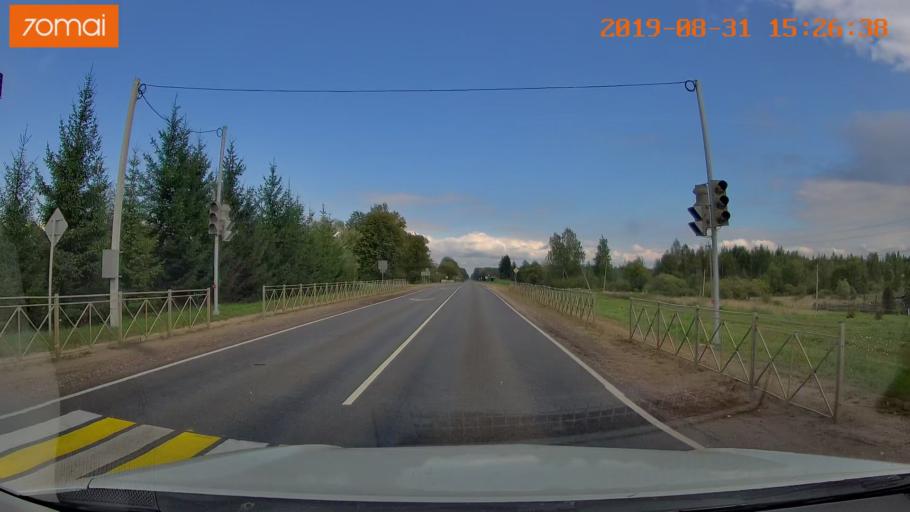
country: RU
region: Kaluga
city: Baryatino
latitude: 54.5515
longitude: 34.5427
